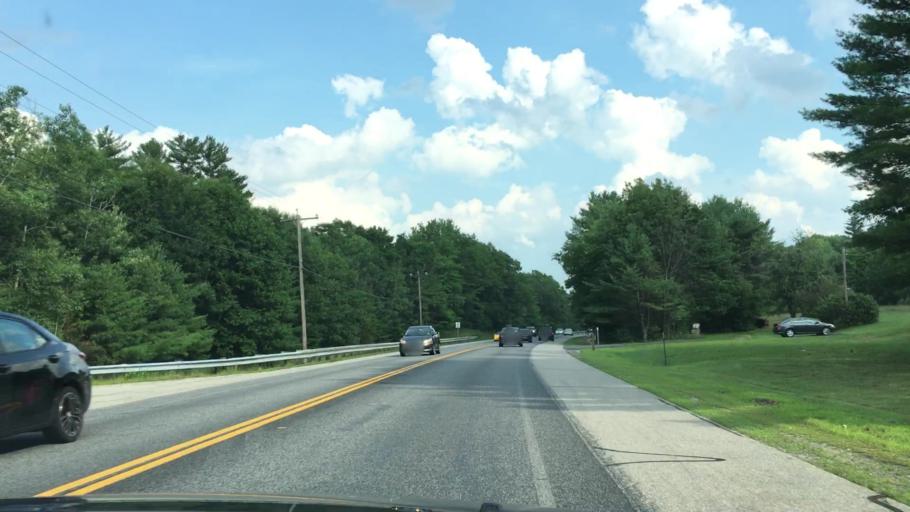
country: US
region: New Hampshire
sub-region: Strafford County
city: Farmington
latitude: 43.3837
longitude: -71.0727
